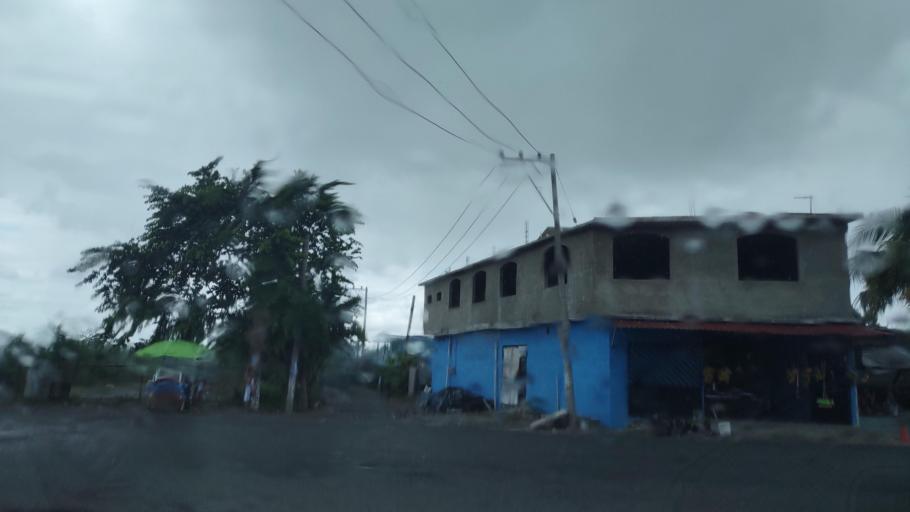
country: MX
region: Veracruz
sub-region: Papantla
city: Residencial Tajin
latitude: 20.6145
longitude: -97.3986
